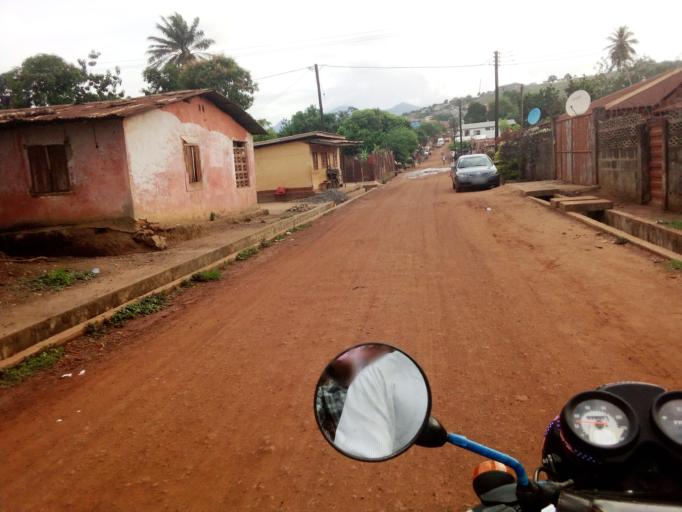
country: SL
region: Western Area
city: Waterloo
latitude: 8.3404
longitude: -13.0716
